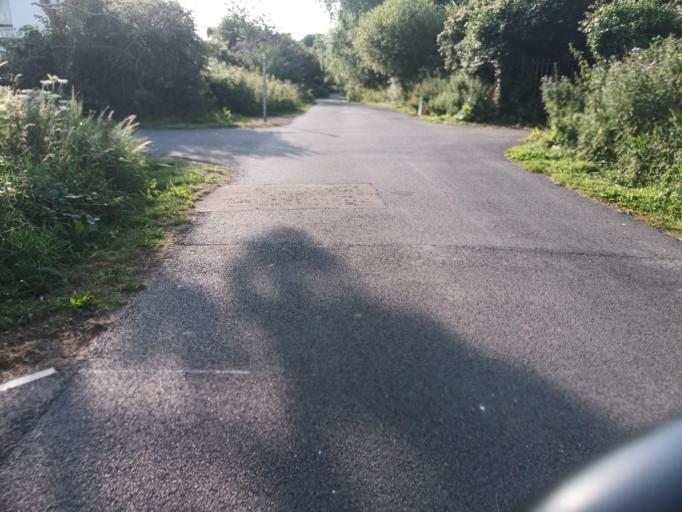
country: GB
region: Northern Ireland
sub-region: Castlereagh District
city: Dundonald
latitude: 54.5889
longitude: -5.8091
